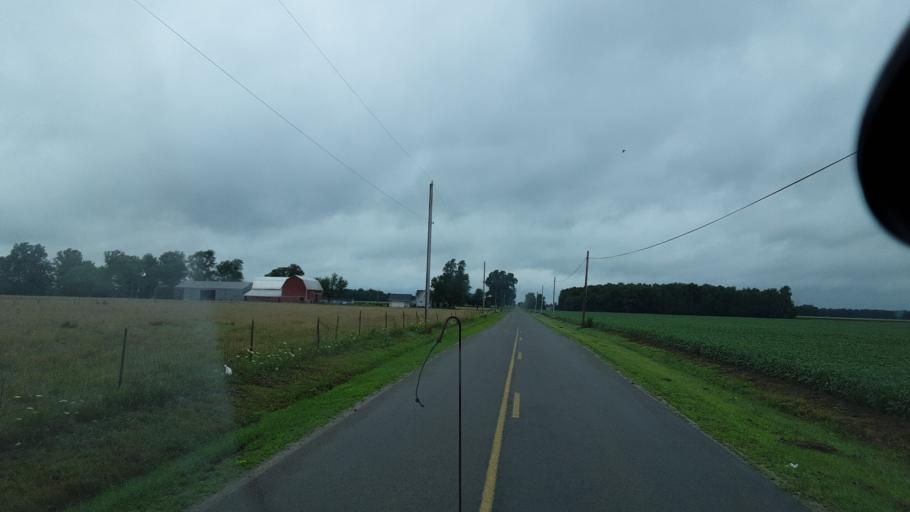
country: US
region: Ohio
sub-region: Van Wert County
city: Convoy
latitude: 40.8228
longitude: -84.7459
